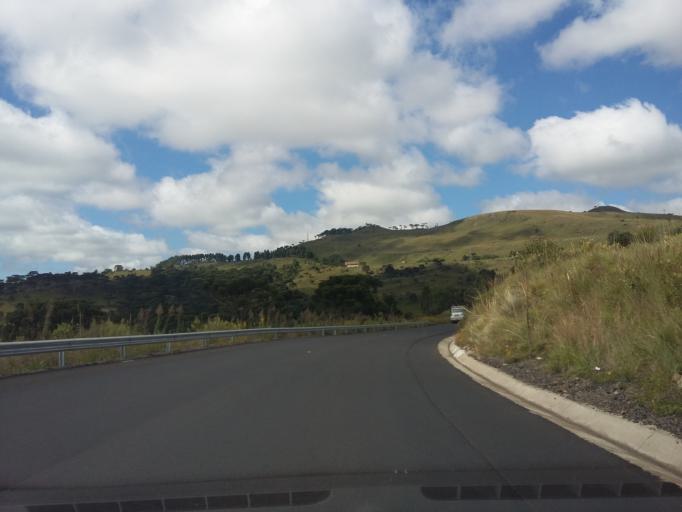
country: BR
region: Santa Catarina
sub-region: Sao Joaquim
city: Sao Joaquim
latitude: -28.1975
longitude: -49.9944
